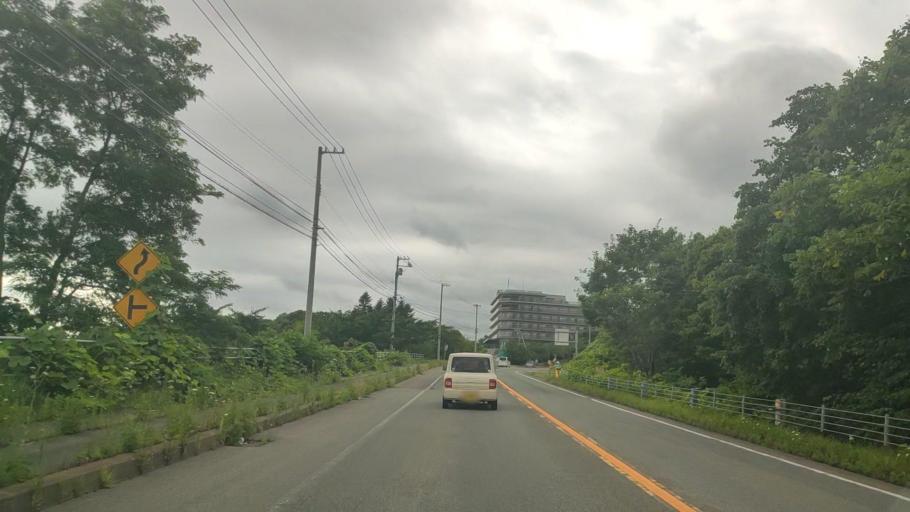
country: JP
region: Hokkaido
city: Date
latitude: 42.5574
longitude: 140.7492
